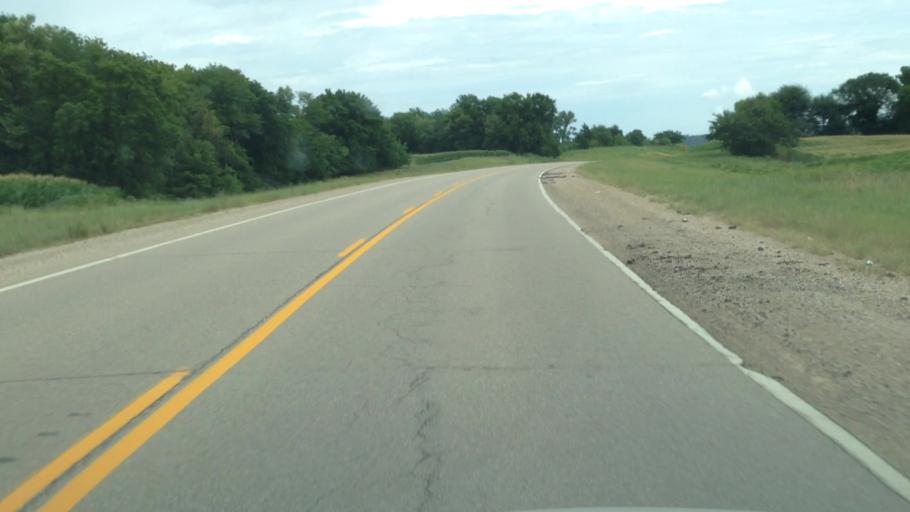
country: US
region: Kansas
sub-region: Jefferson County
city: Oskaloosa
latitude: 39.0928
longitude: -95.4754
